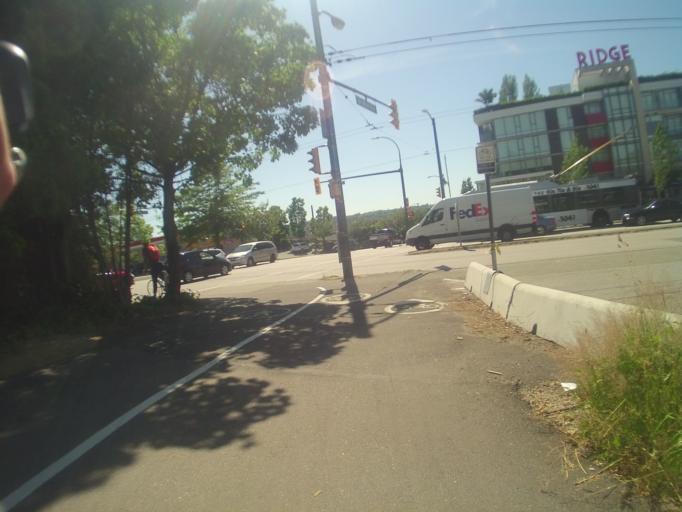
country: CA
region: British Columbia
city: West End
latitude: 49.2574
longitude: -123.1527
